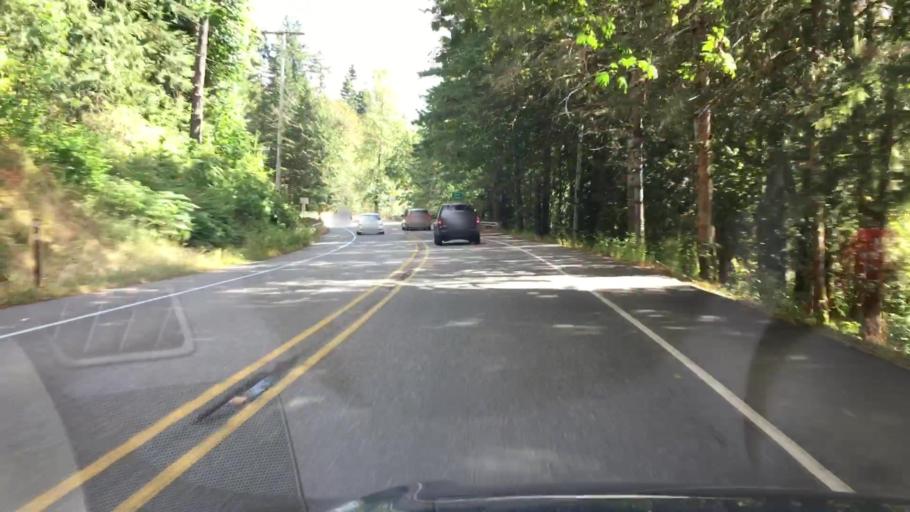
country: US
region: Washington
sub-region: Pierce County
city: Eatonville
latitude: 46.7522
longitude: -121.9419
